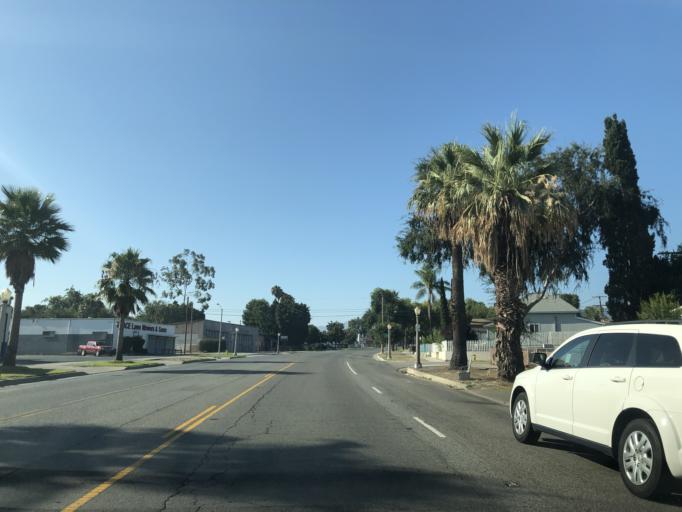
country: US
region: California
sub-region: Riverside County
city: Corona
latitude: 33.8773
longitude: -117.5592
